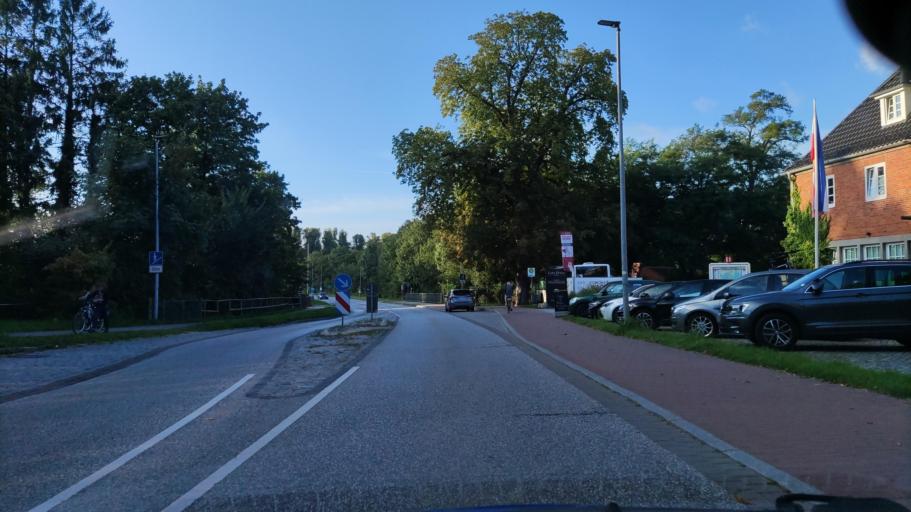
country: DE
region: Schleswig-Holstein
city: Ploen
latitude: 54.1529
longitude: 10.4501
